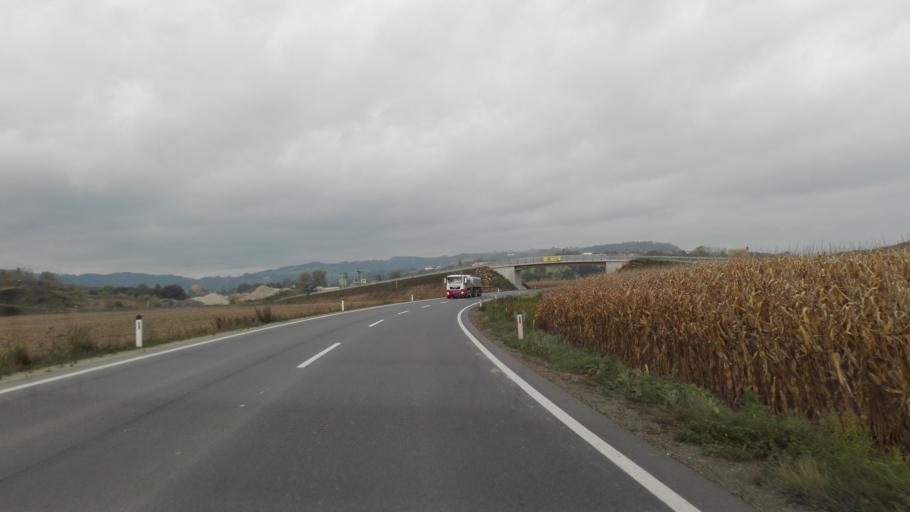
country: AT
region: Upper Austria
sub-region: Politischer Bezirk Urfahr-Umgebung
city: Feldkirchen an der Donau
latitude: 48.2993
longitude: 14.0042
